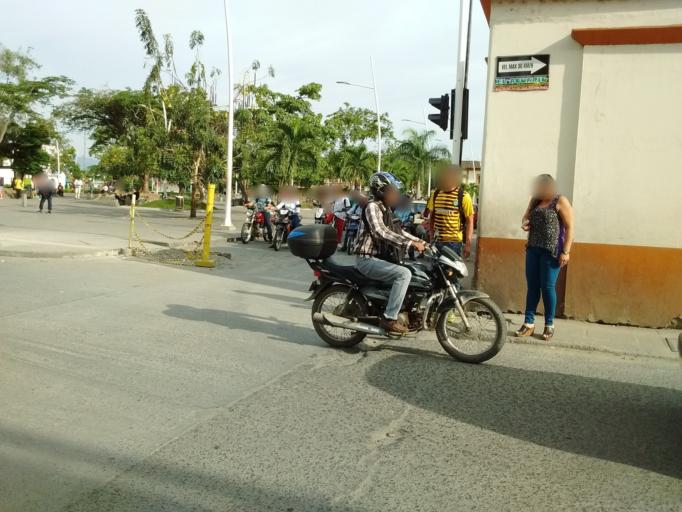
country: CO
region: Valle del Cauca
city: Tulua
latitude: 4.0851
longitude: -76.1969
